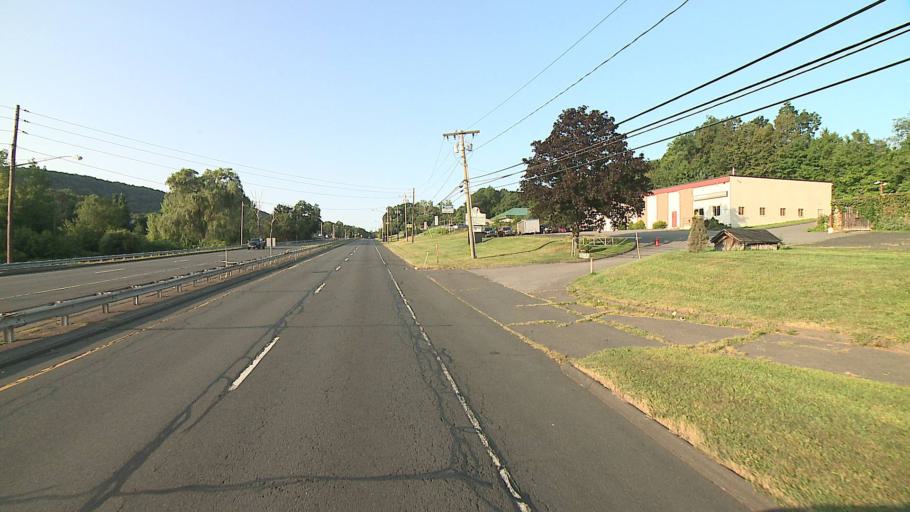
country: US
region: Connecticut
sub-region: Hartford County
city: Kensington
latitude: 41.5912
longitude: -72.7587
